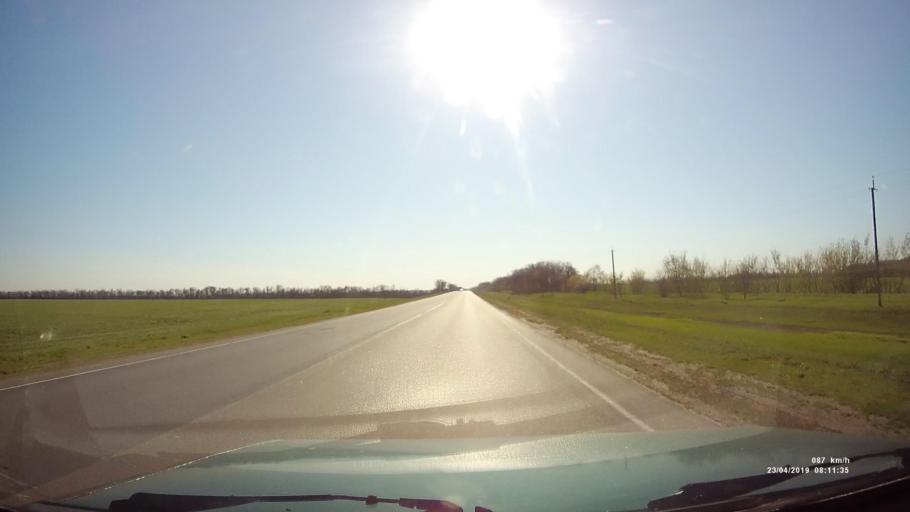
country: RU
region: Rostov
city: Yegorlykskaya
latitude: 46.5534
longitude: 40.7017
